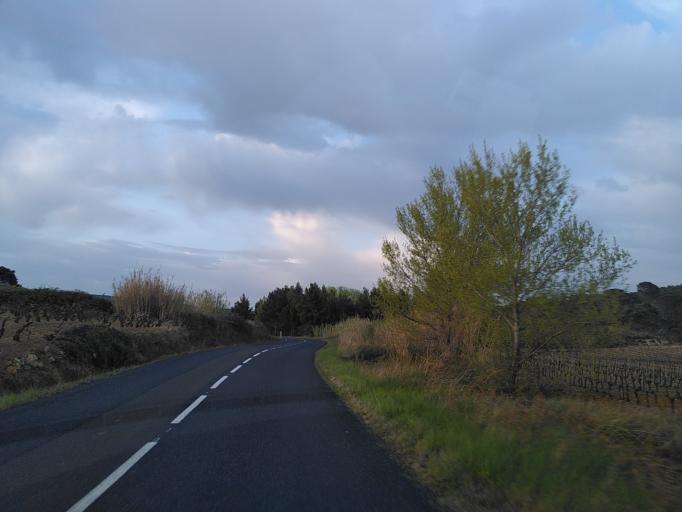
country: FR
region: Languedoc-Roussillon
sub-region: Departement des Pyrenees-Orientales
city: Estagel
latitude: 42.8040
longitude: 2.6987
